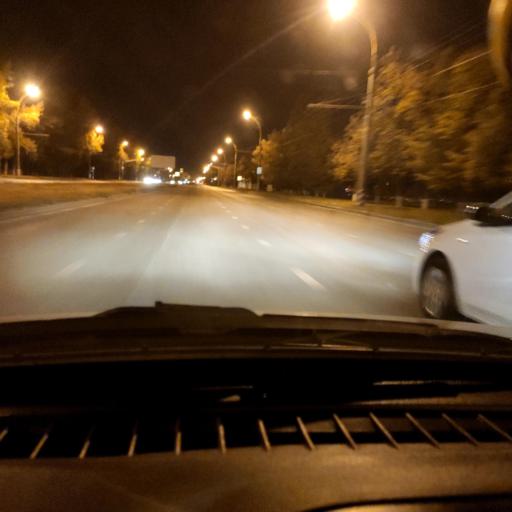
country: RU
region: Samara
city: Tol'yatti
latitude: 53.5130
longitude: 49.2574
